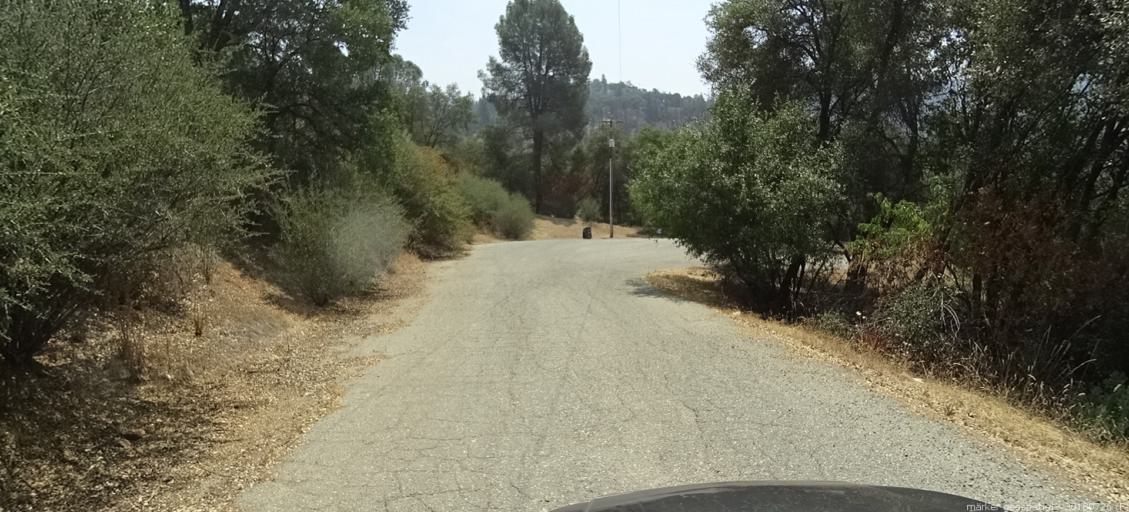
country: US
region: California
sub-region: Madera County
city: Oakhurst
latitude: 37.2915
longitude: -119.6469
